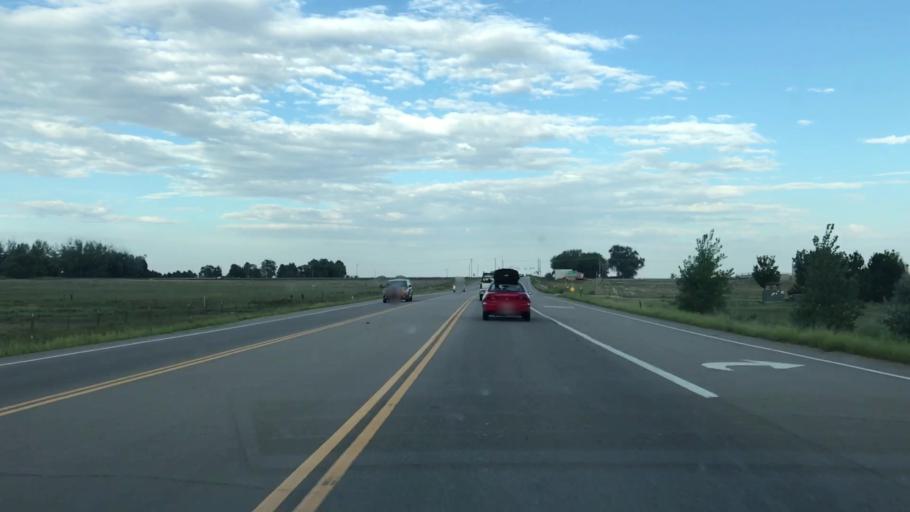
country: US
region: Colorado
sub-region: Weld County
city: Mead
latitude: 40.2041
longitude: -105.0047
